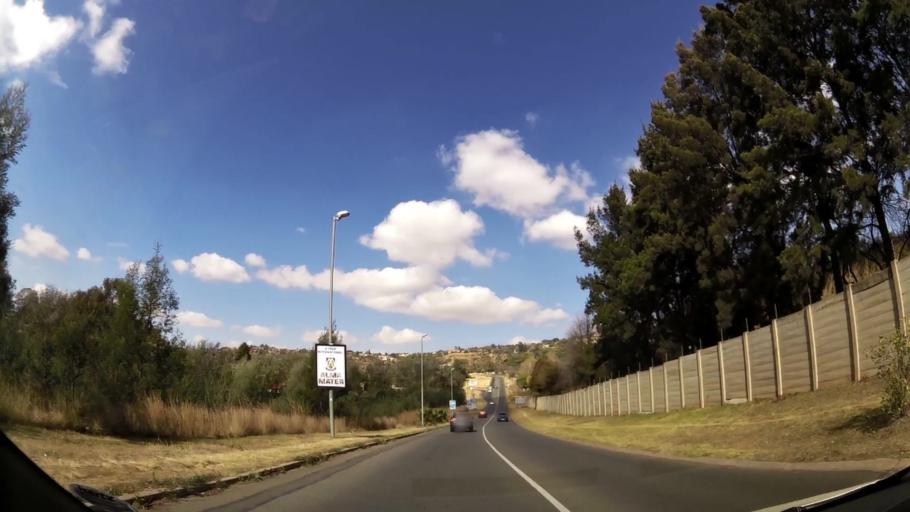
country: ZA
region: Gauteng
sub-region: City of Johannesburg Metropolitan Municipality
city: Roodepoort
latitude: -26.1060
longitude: 27.8387
